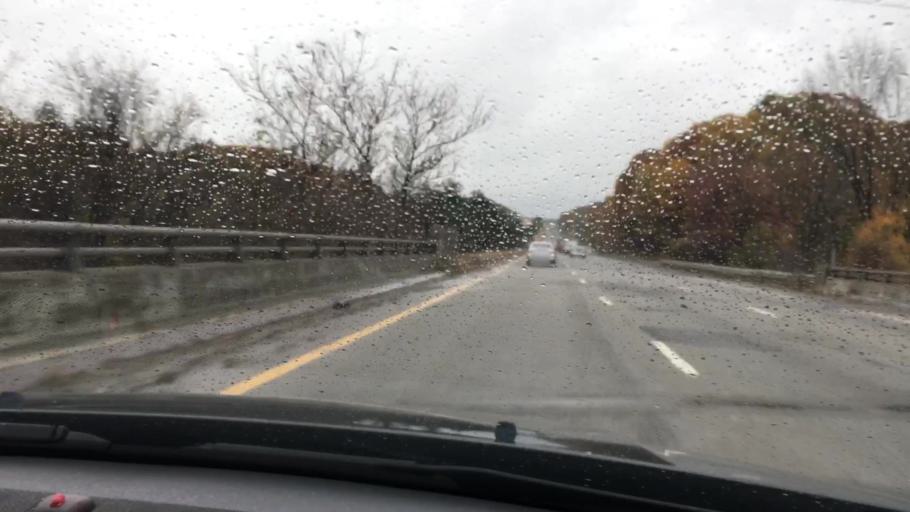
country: US
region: Massachusetts
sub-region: Middlesex County
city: Littleton Common
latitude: 42.5556
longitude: -71.4518
